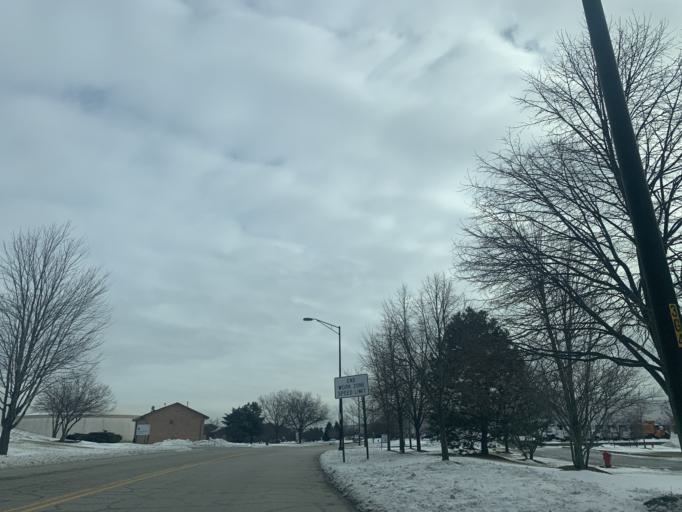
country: US
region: Illinois
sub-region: Will County
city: Romeoville
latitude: 41.6679
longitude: -88.1224
